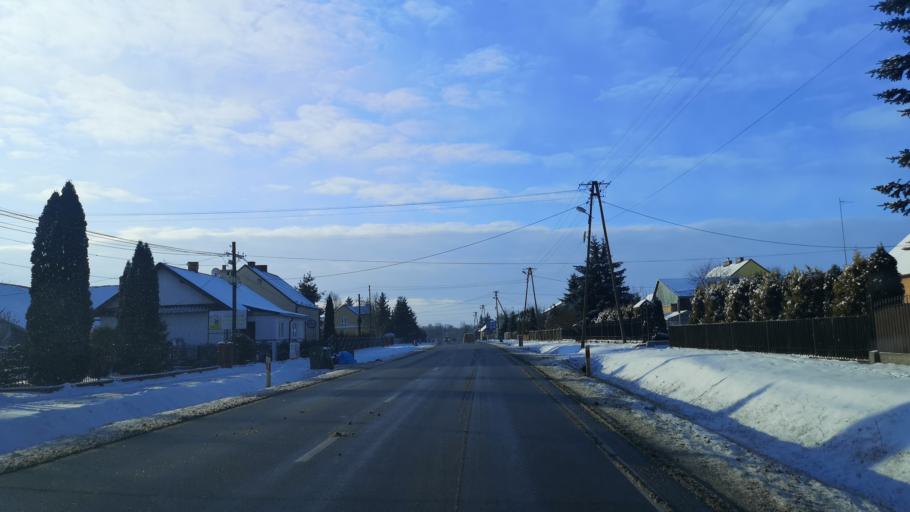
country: PL
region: Subcarpathian Voivodeship
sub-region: Powiat przeworski
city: Gorliczyna
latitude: 50.1015
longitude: 22.4950
